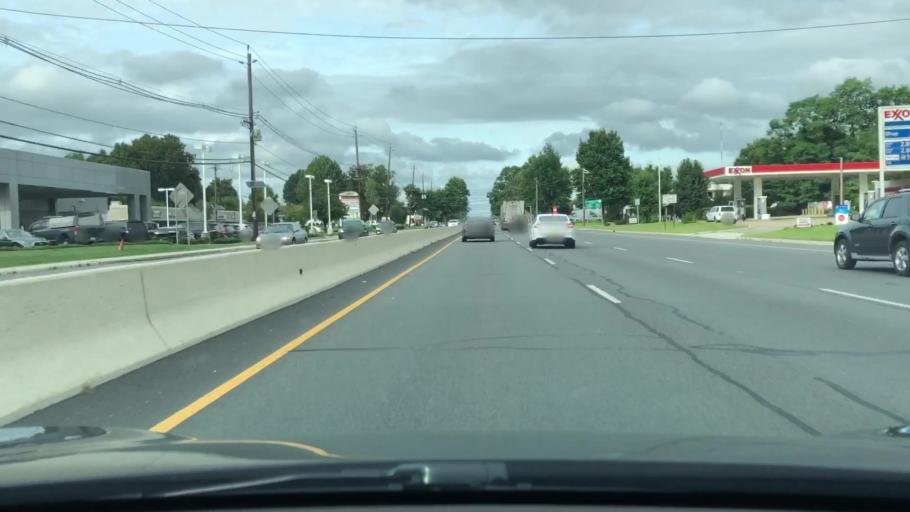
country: US
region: New Jersey
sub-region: Mercer County
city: Lawrenceville
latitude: 40.2706
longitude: -74.7116
